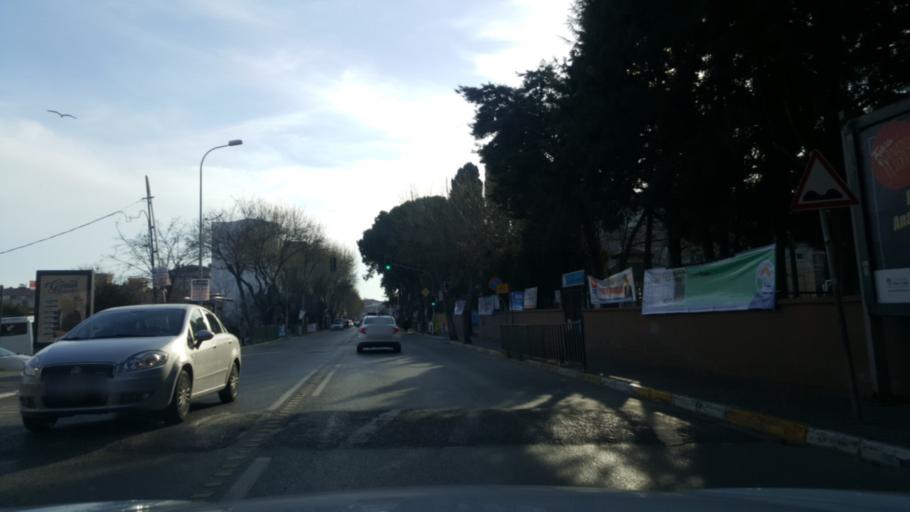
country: TR
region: Istanbul
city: Icmeler
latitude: 40.8208
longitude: 29.3082
